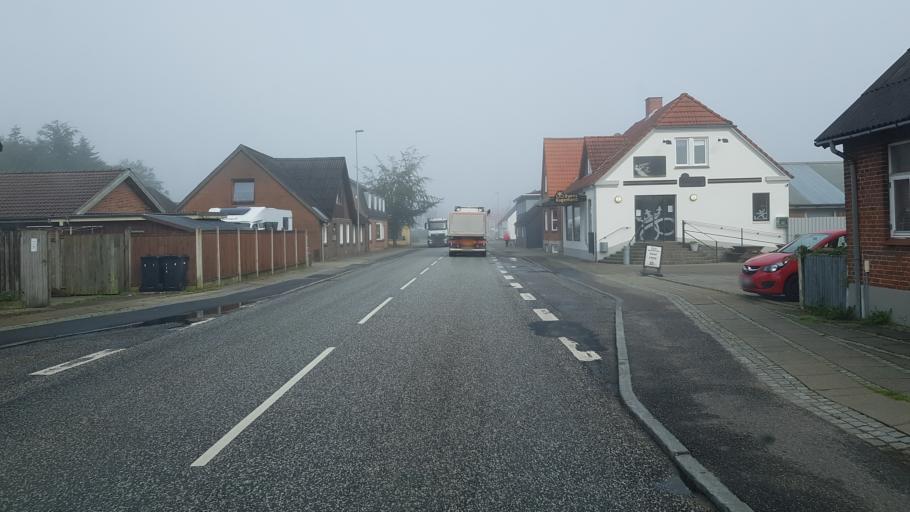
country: DK
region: Central Jutland
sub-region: Viborg Kommune
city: Karup
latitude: 56.3383
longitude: 9.2540
